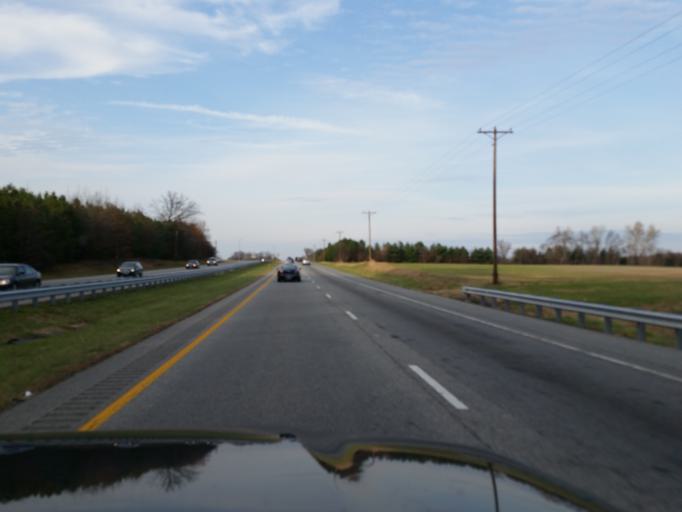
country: US
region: Maryland
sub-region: Talbot County
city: Easton
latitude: 38.9024
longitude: -76.0617
